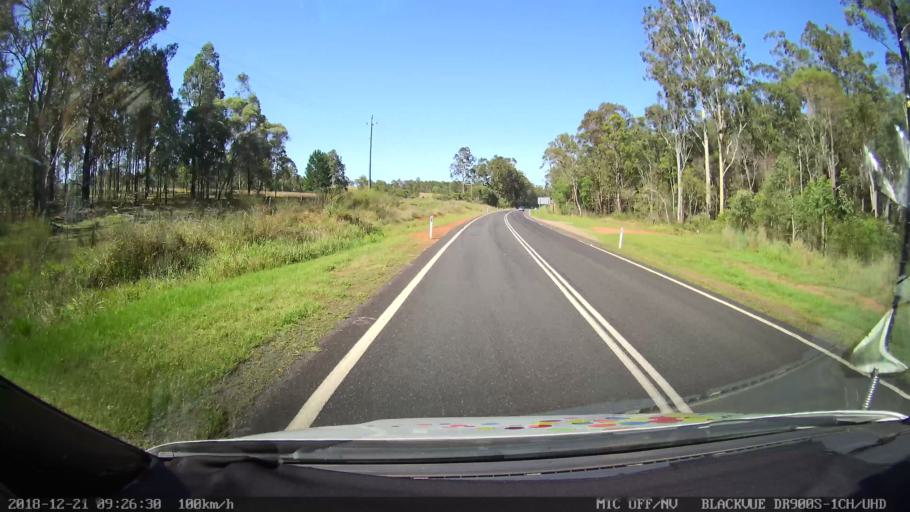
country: AU
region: New South Wales
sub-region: Clarence Valley
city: Maclean
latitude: -29.3936
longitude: 153.0016
